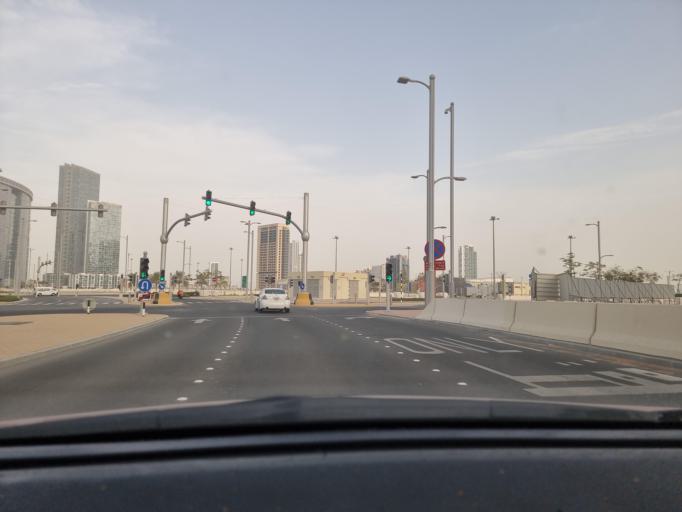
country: AE
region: Abu Dhabi
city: Abu Dhabi
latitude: 24.4969
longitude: 54.3961
